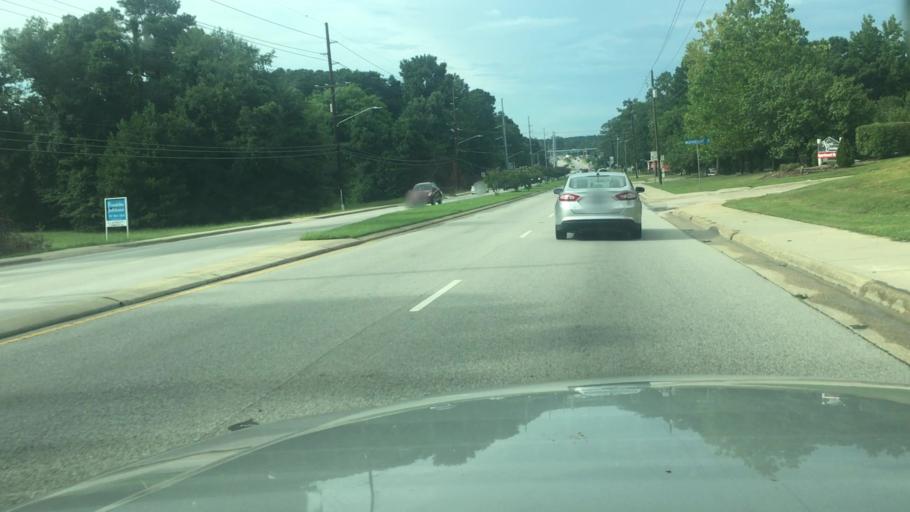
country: US
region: North Carolina
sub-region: Cumberland County
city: Eastover
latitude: 35.1451
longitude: -78.8720
